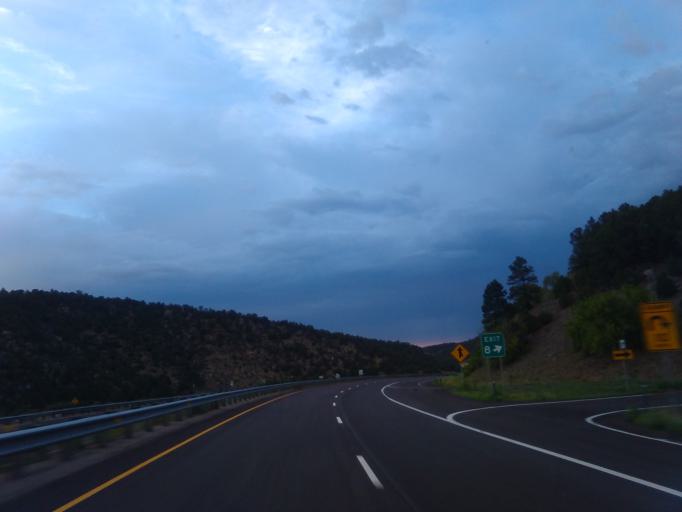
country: US
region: Colorado
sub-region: Las Animas County
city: Trinidad
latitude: 37.0868
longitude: -104.5223
